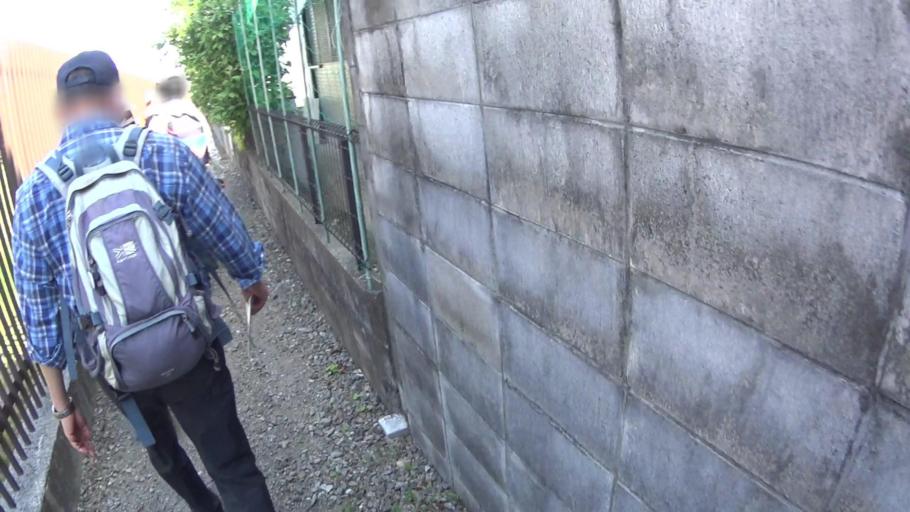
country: JP
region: Osaka
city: Kashihara
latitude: 34.5733
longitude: 135.6176
